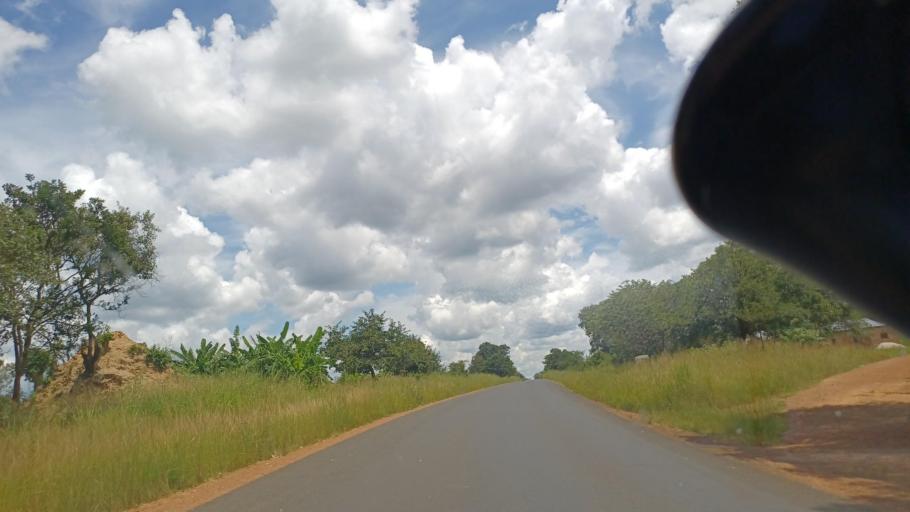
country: ZM
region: North-Western
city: Solwezi
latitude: -12.4071
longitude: 26.2393
